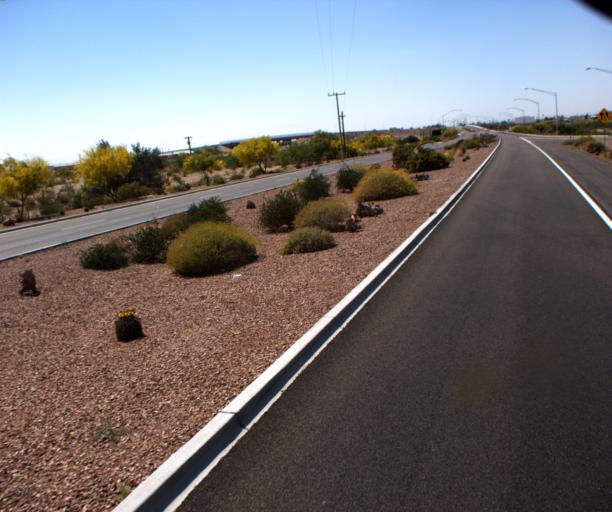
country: US
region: Arizona
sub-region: Maricopa County
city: Gila Bend
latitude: 32.9533
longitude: -112.6899
